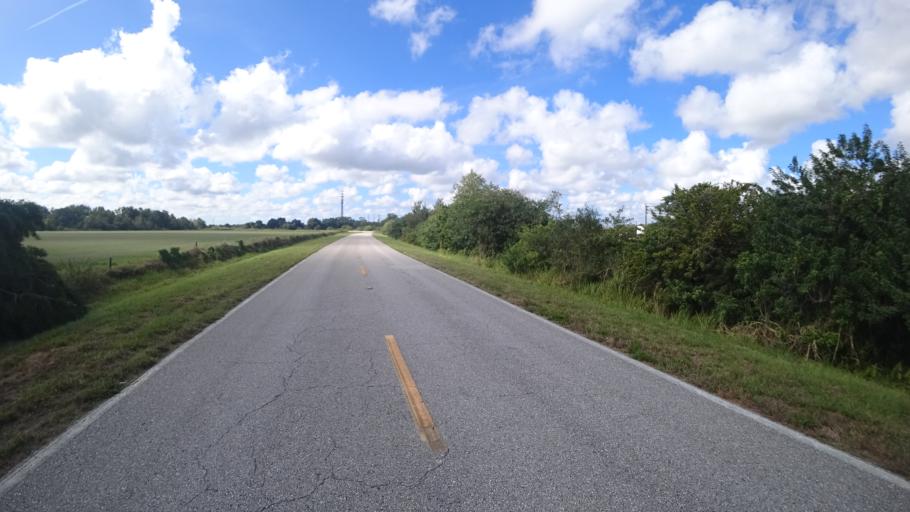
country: US
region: Florida
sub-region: Manatee County
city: Ellenton
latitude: 27.6199
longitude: -82.4795
